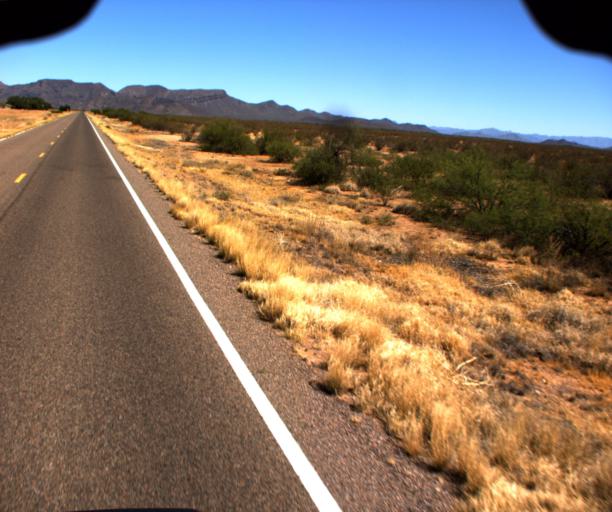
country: US
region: Arizona
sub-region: Yavapai County
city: Congress
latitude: 33.9633
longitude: -113.1415
